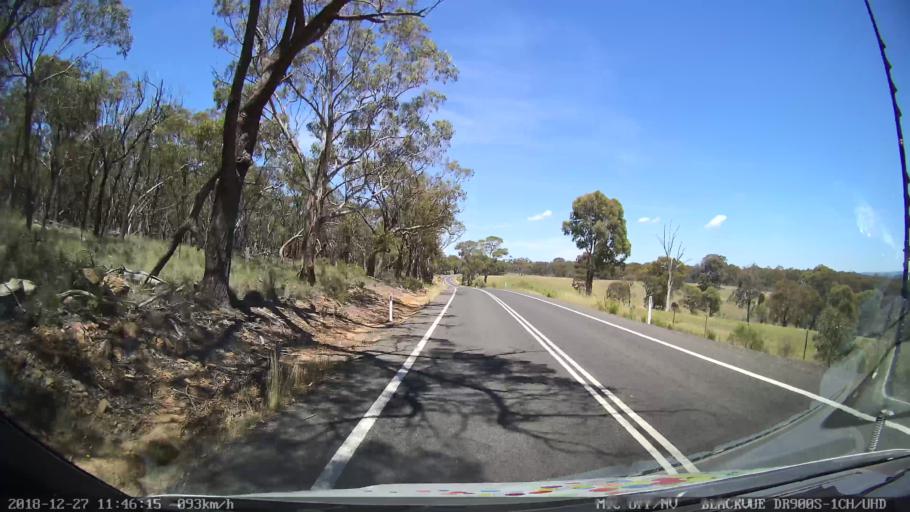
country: AU
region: New South Wales
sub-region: Bathurst Regional
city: Perthville
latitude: -33.5888
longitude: 149.4602
